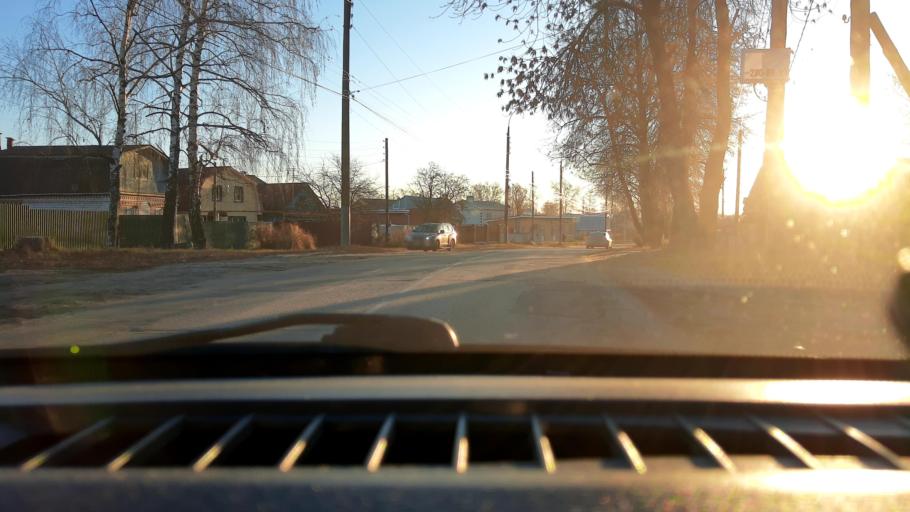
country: RU
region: Nizjnij Novgorod
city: Kstovo
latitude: 56.1812
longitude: 44.1680
